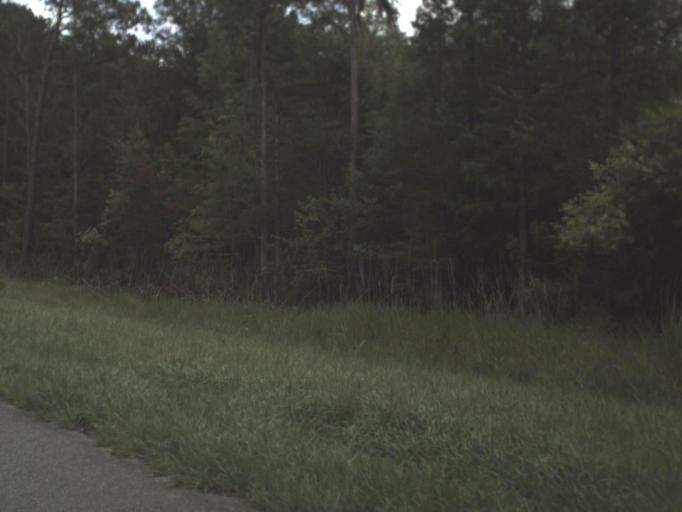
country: US
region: Florida
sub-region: Madison County
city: Madison
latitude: 30.4867
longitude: -83.5206
